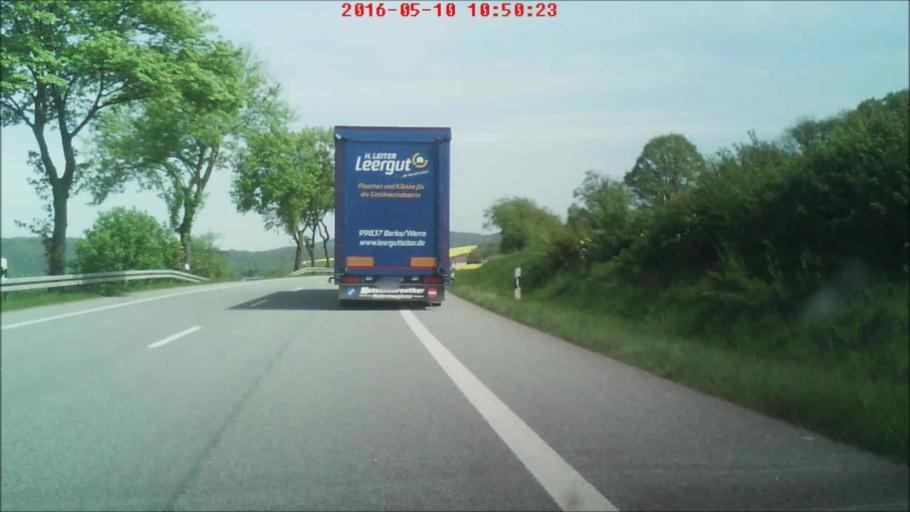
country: DE
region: Hesse
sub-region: Regierungsbezirk Kassel
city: Burghaun
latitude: 50.7753
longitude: 9.7021
